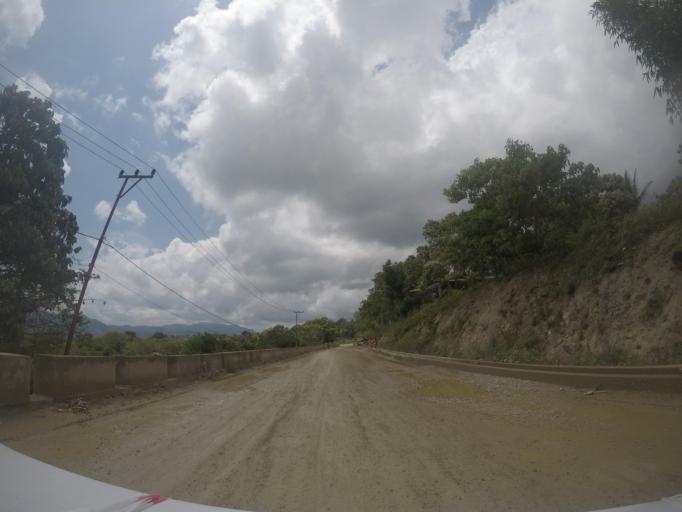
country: TL
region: Baucau
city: Venilale
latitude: -8.5863
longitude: 126.3879
